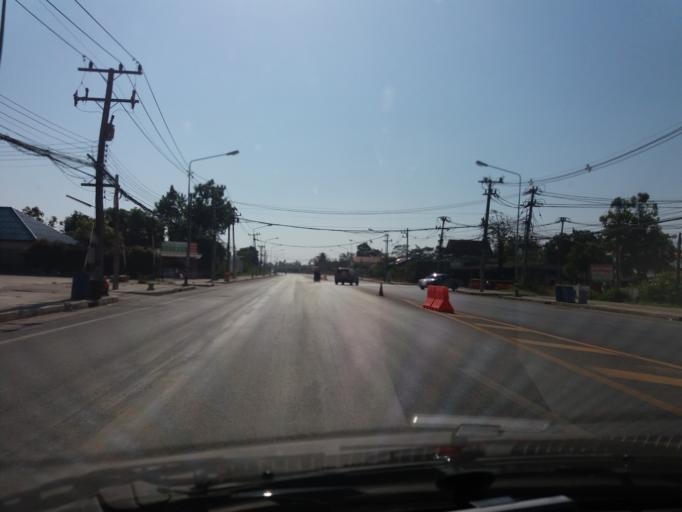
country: TH
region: Kamphaeng Phet
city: Khlong Khlung
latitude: 16.2183
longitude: 99.7298
